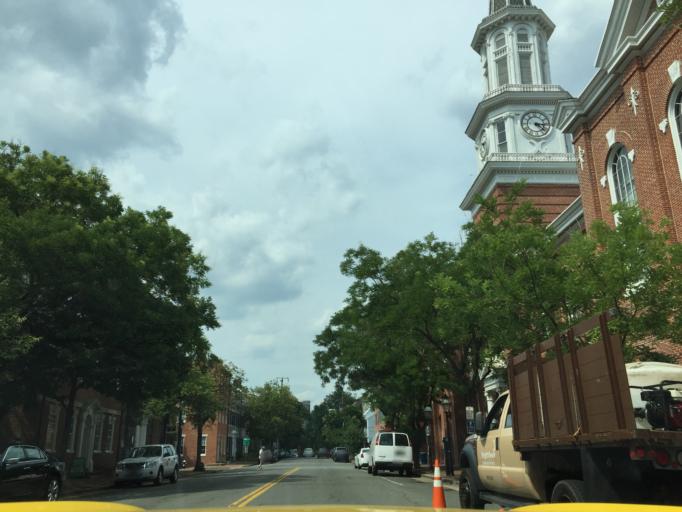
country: US
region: Virginia
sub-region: City of Alexandria
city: Alexandria
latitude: 38.8052
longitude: -77.0435
